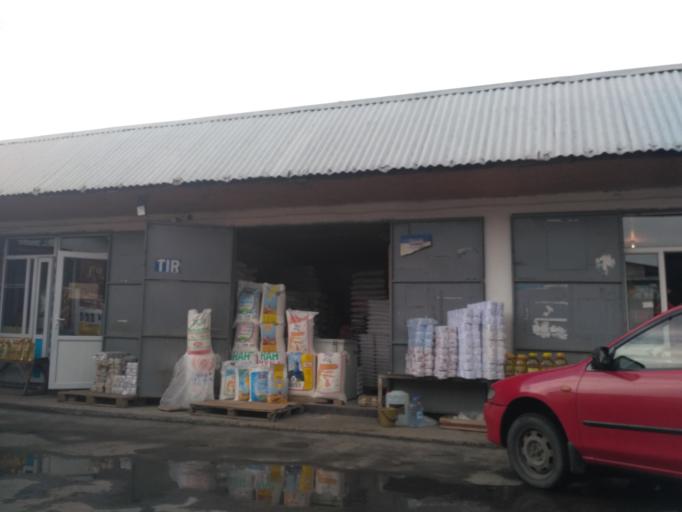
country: KZ
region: Almaty Oblysy
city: Burunday
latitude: 43.2031
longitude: 76.6349
